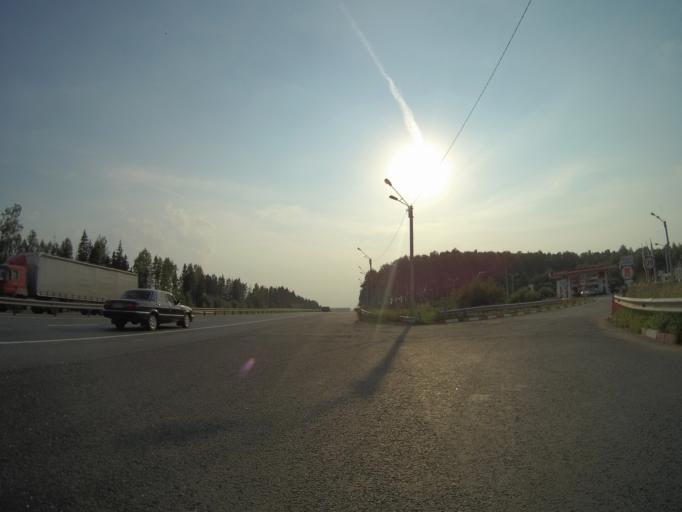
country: RU
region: Vladimir
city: Melekhovo
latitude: 56.2113
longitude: 41.3029
